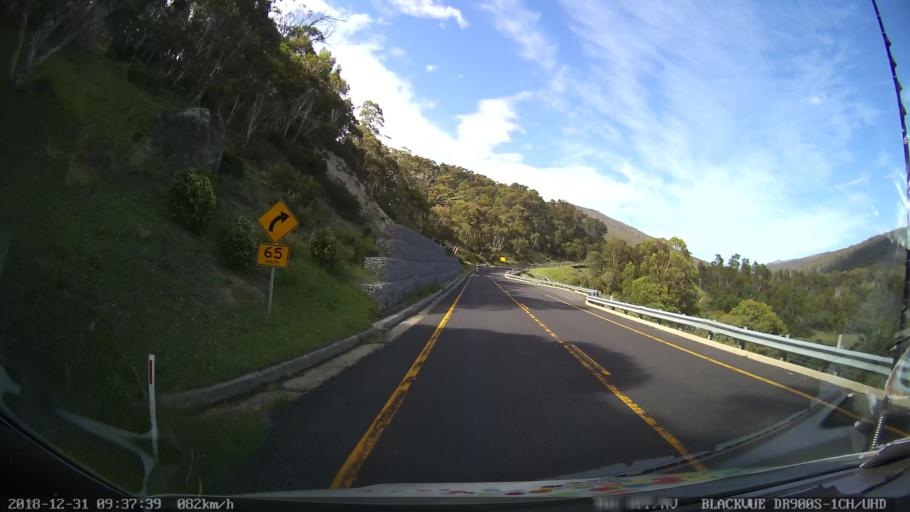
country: AU
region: New South Wales
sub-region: Snowy River
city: Jindabyne
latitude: -36.4684
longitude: 148.3743
